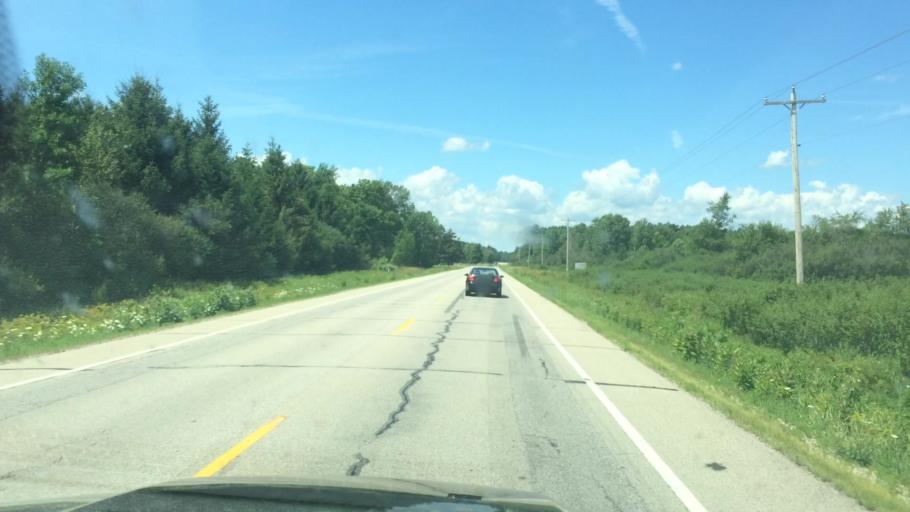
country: US
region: Wisconsin
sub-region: Marinette County
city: Peshtigo
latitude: 45.1001
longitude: -87.7192
